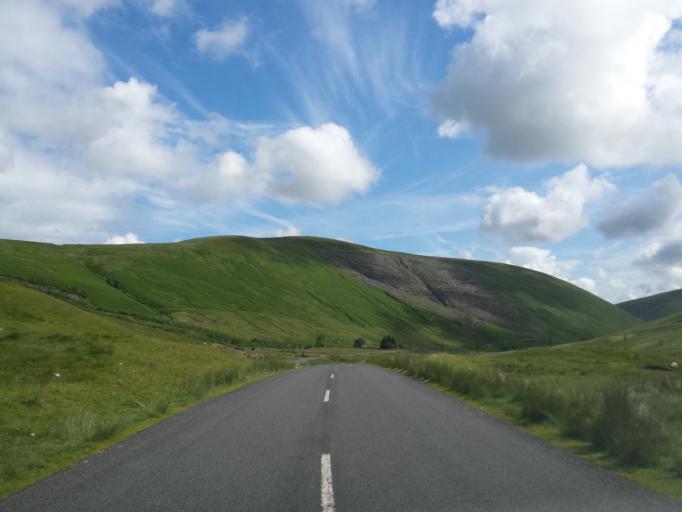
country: GB
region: Scotland
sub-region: Dumfries and Galloway
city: Moffat
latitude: 55.4348
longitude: -3.2591
